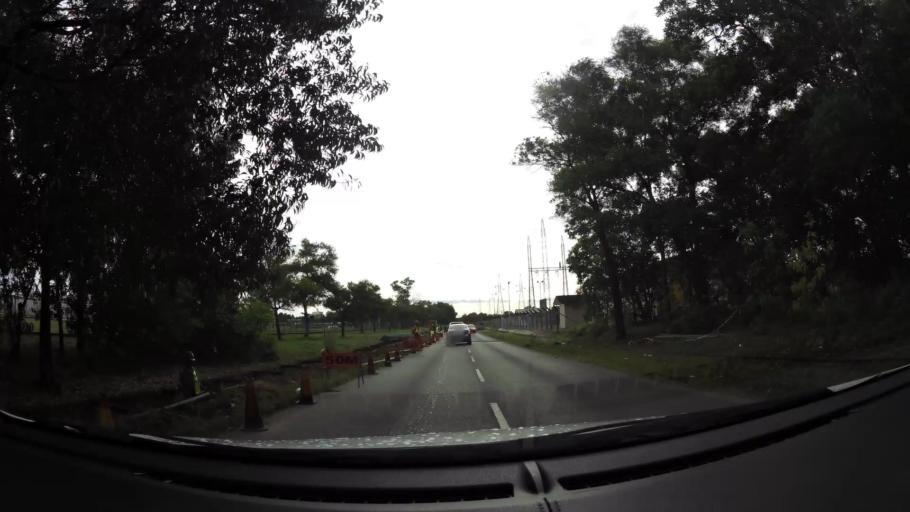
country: BN
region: Belait
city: Seria
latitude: 4.6161
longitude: 114.3428
